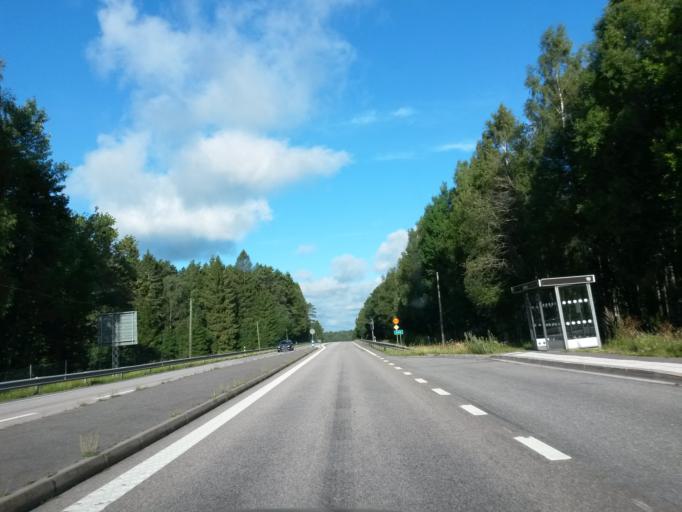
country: SE
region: Vaestra Goetaland
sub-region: Vargarda Kommun
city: Jonstorp
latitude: 58.0064
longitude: 12.7577
